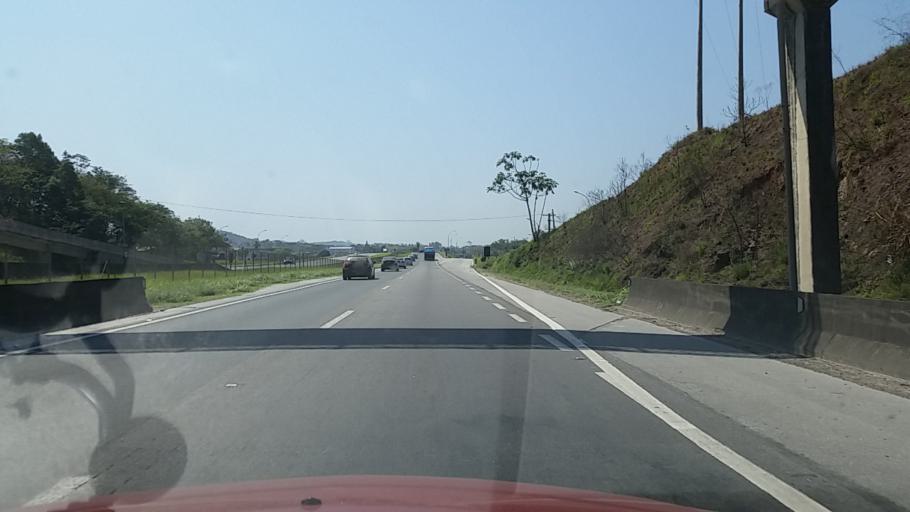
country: BR
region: Sao Paulo
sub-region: Miracatu
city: Miracatu
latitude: -24.2902
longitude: -47.4641
